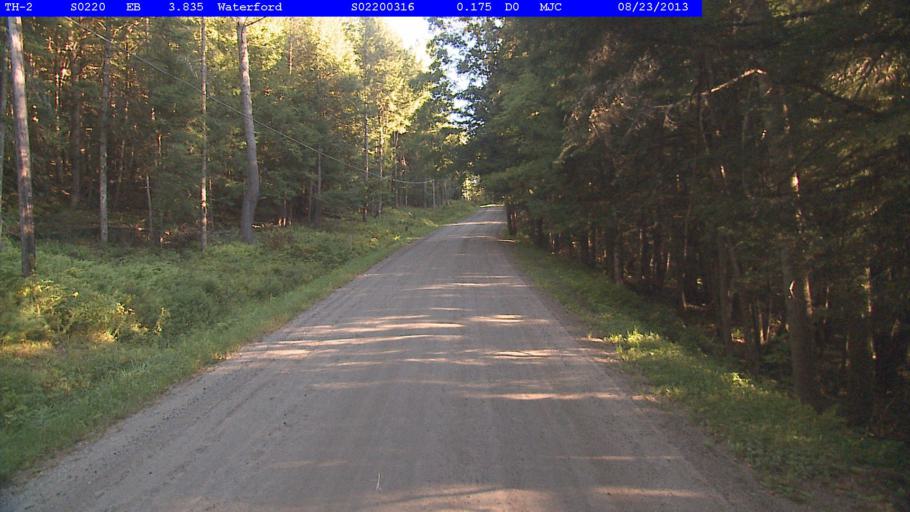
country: US
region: Vermont
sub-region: Caledonia County
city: Saint Johnsbury
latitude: 44.3432
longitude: -71.9891
